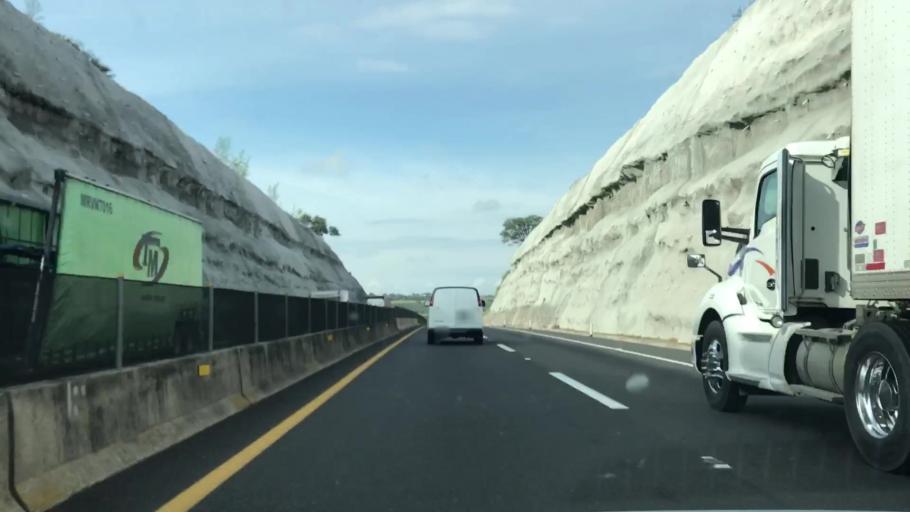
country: MX
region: Jalisco
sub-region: San Juan de los Lagos
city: Mezquitic de la Magdalena
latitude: 21.1968
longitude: -102.3419
